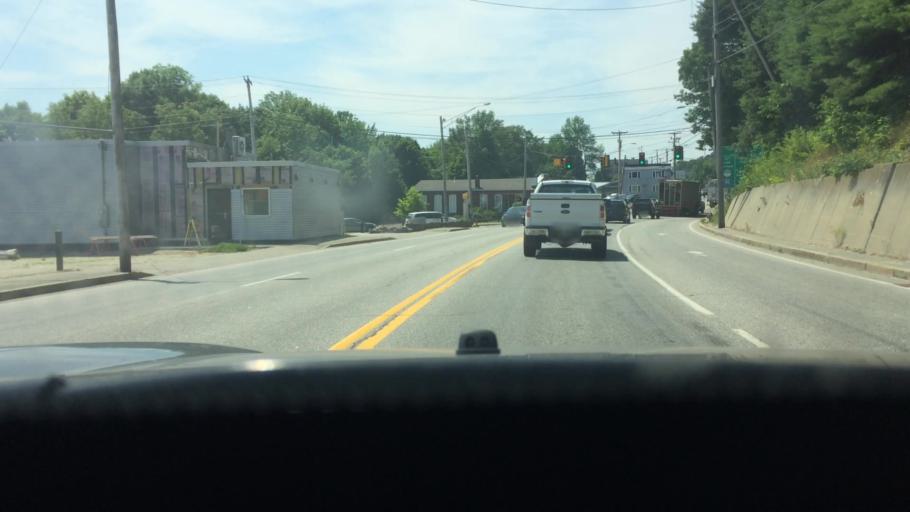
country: US
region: Maine
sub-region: Androscoggin County
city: Auburn
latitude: 44.0917
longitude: -70.2305
